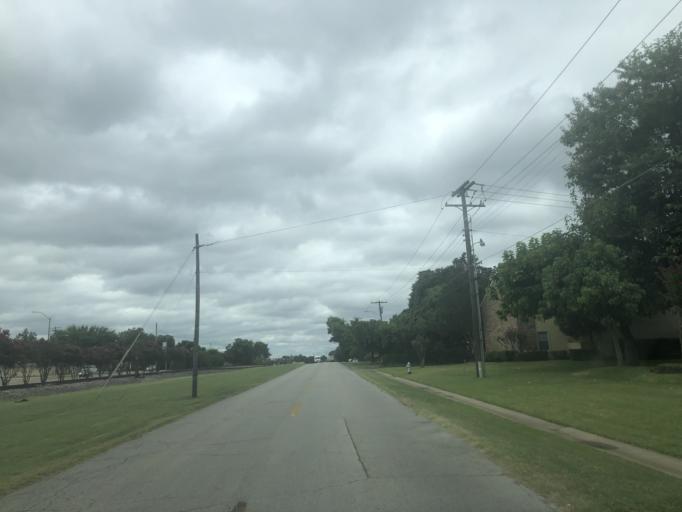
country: US
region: Texas
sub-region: Dallas County
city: Duncanville
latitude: 32.6608
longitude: -96.9074
